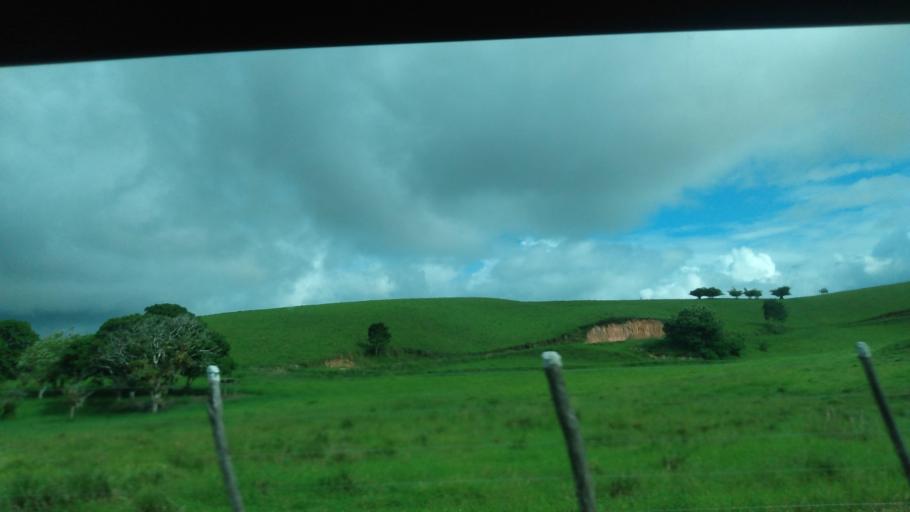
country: BR
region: Pernambuco
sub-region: Quipapa
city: Quipapa
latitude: -8.7771
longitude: -35.9241
